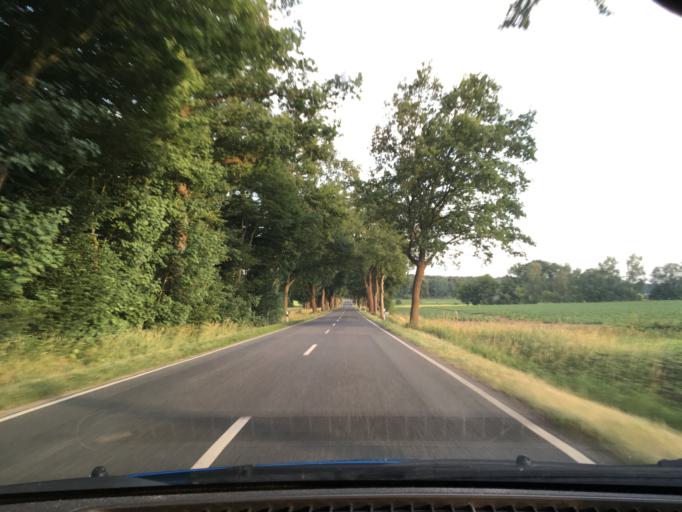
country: DE
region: Lower Saxony
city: Eldingen
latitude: 52.7141
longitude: 10.3177
